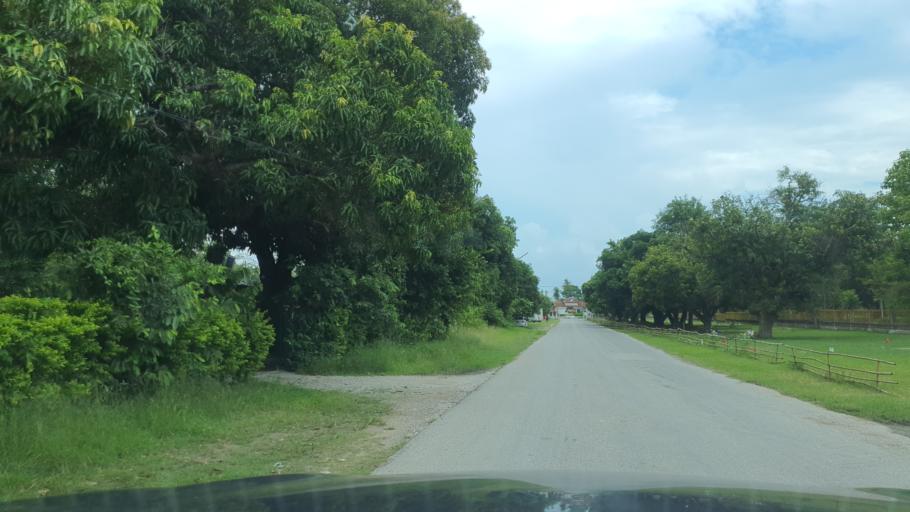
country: TH
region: Chiang Mai
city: Chiang Mai
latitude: 18.8223
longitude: 98.9779
